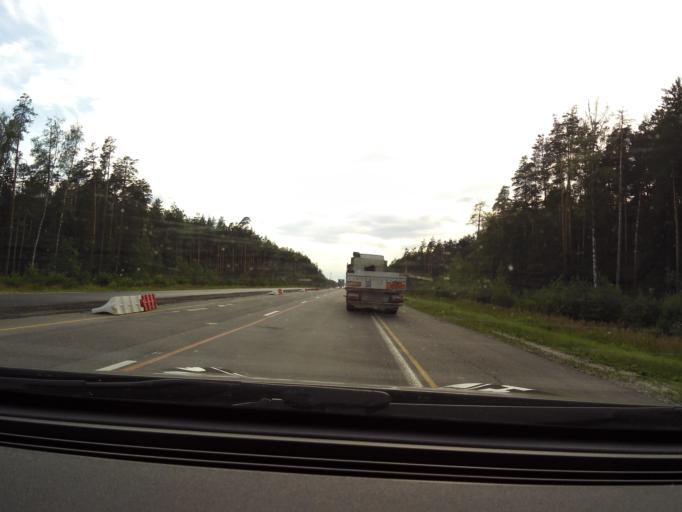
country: RU
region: Vladimir
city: Orgtrud
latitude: 56.1029
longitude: 40.7256
